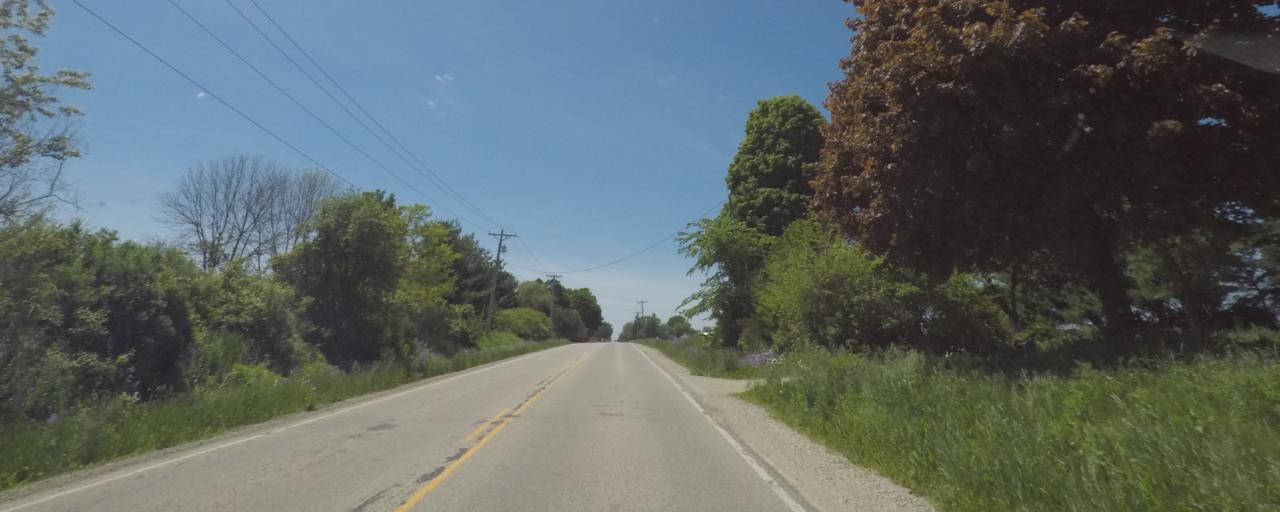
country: US
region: Wisconsin
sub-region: Rock County
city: Evansville
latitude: 42.7876
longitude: -89.3339
